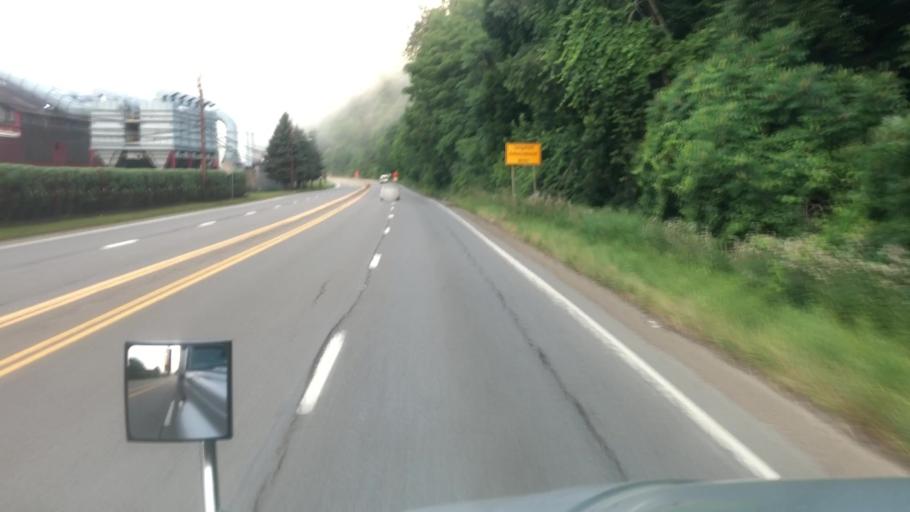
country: US
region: Pennsylvania
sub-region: Venango County
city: Oil City
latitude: 41.4319
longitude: -79.7164
